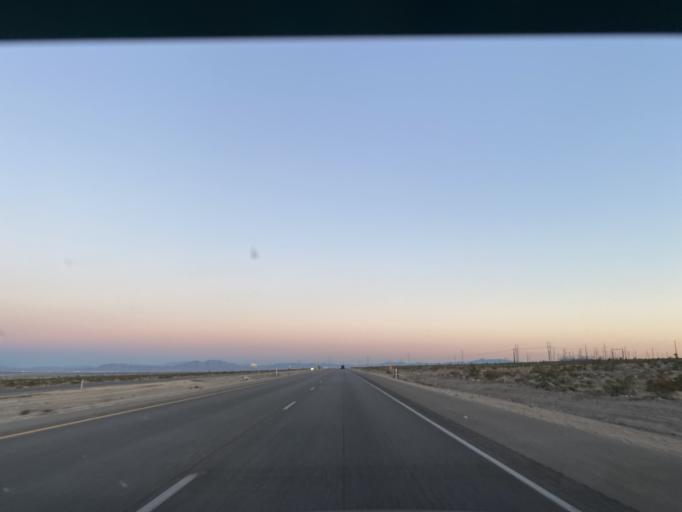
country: US
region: Nevada
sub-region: Clark County
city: Summerlin South
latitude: 36.3500
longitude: -115.3371
